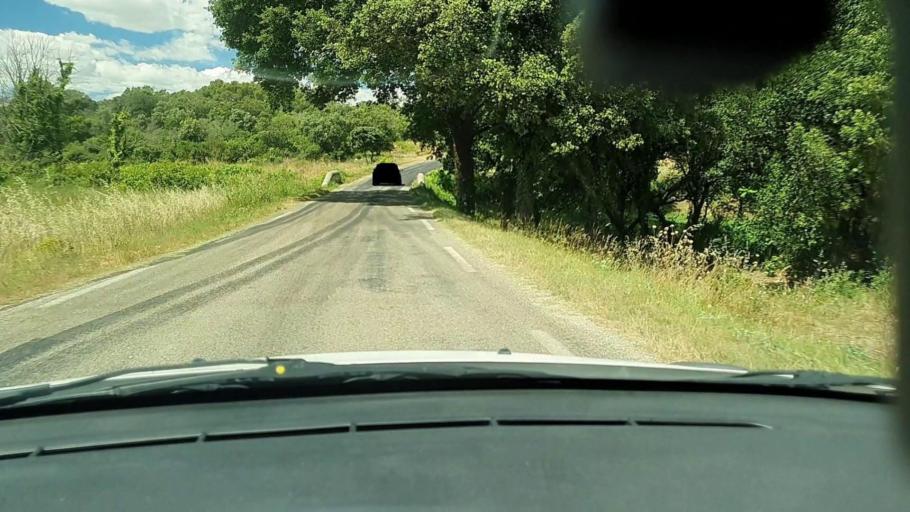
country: FR
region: Languedoc-Roussillon
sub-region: Departement du Gard
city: Cabrieres
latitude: 43.9549
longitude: 4.4490
